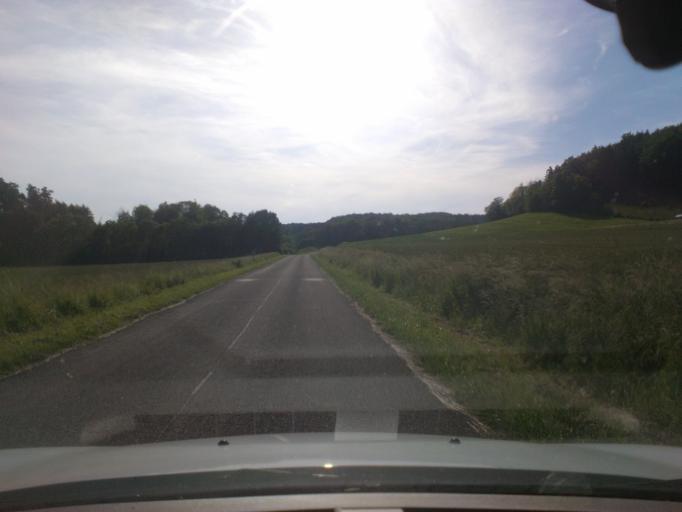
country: FR
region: Lorraine
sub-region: Departement des Vosges
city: Mirecourt
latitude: 48.2672
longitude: 6.2125
